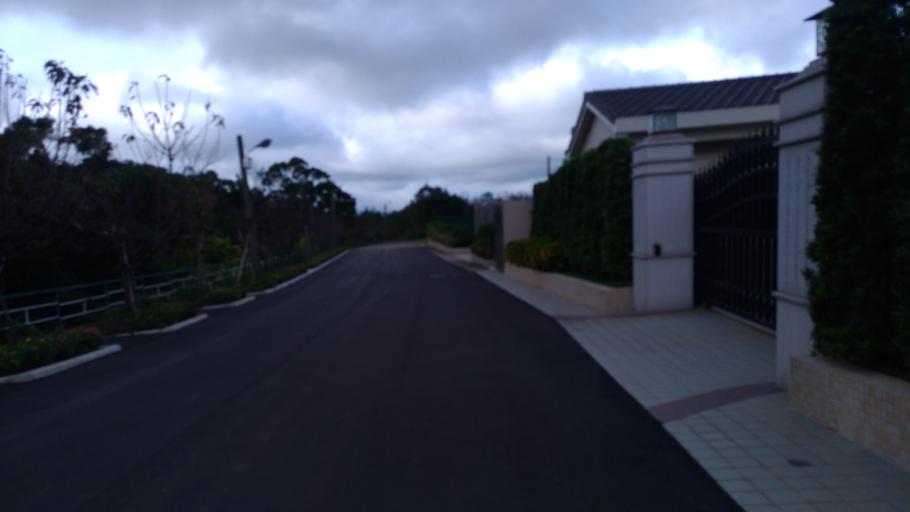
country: TW
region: Taiwan
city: Daxi
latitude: 24.8875
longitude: 121.1716
